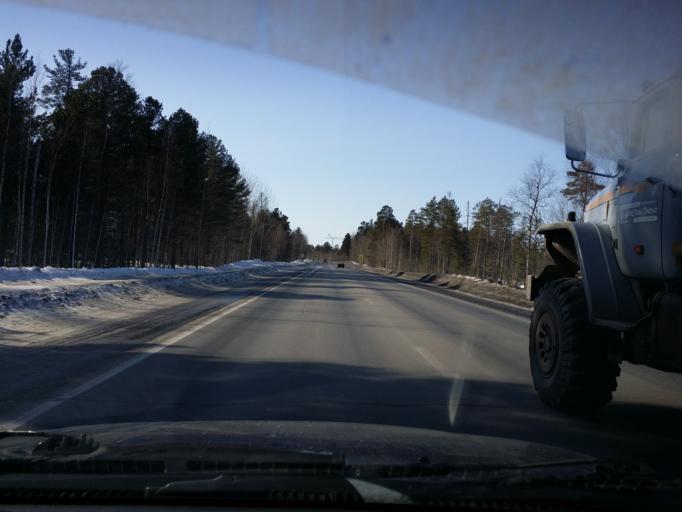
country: RU
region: Khanty-Mansiyskiy Avtonomnyy Okrug
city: Megion
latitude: 61.1625
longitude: 75.6997
